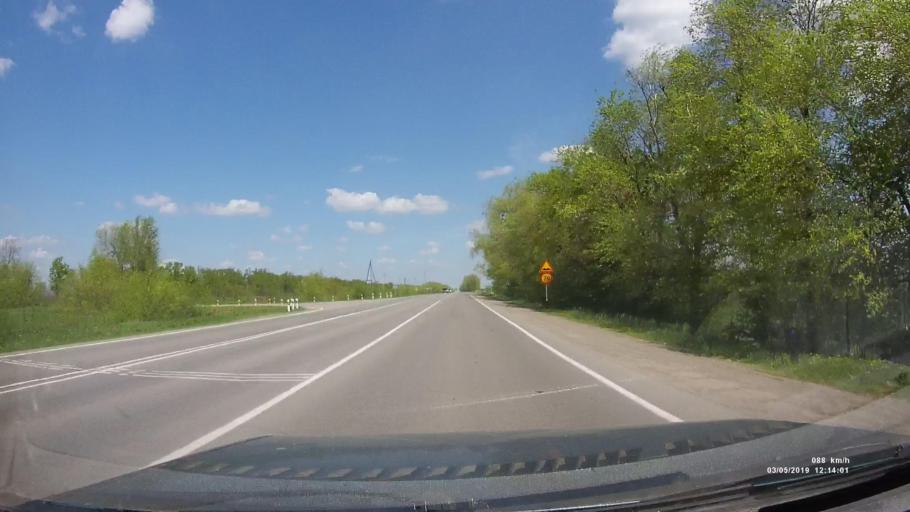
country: RU
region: Rostov
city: Melikhovskaya
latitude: 47.3384
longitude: 40.5592
